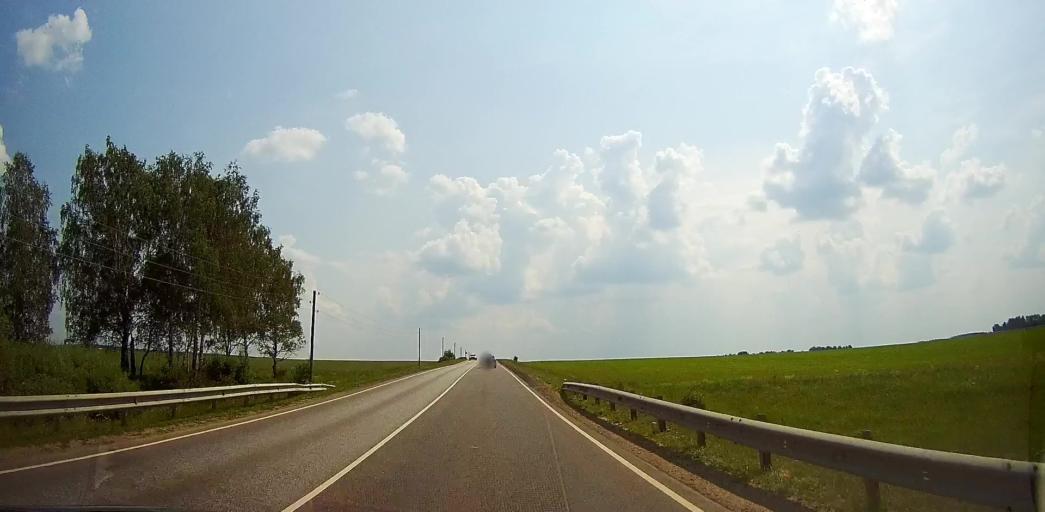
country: RU
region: Moskovskaya
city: Malino
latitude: 55.0421
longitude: 38.1520
